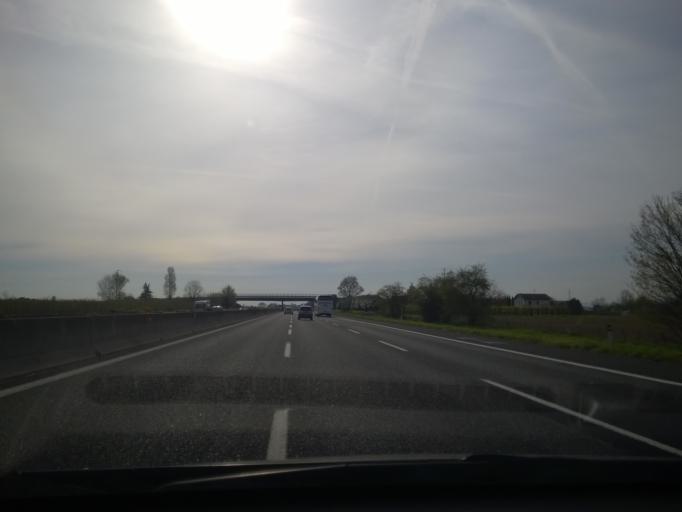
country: IT
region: Emilia-Romagna
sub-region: Forli-Cesena
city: Forli
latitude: 44.2638
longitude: 12.0568
